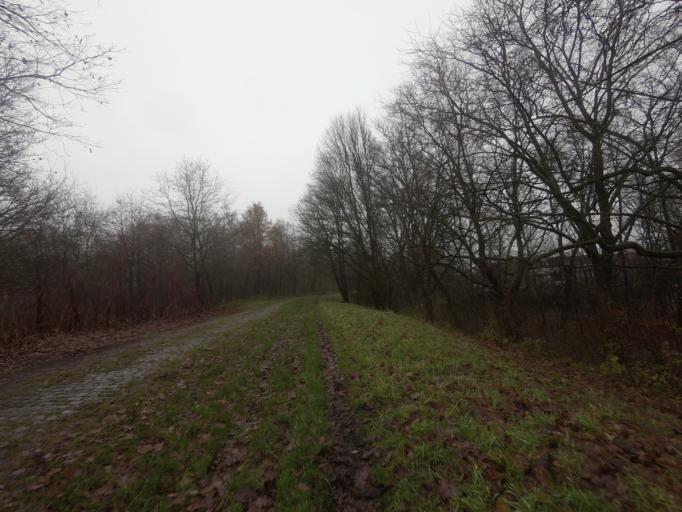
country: BE
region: Flanders
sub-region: Provincie Antwerpen
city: Hoboken
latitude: 51.1843
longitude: 4.3348
